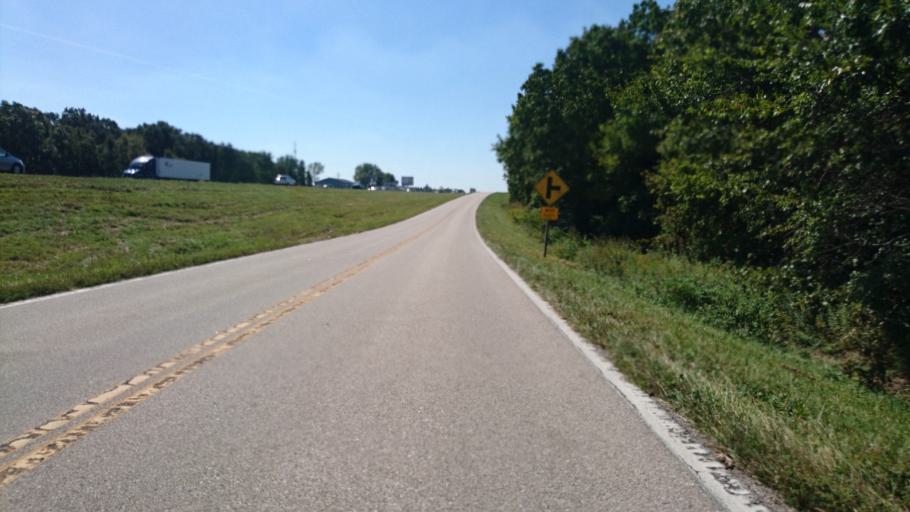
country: US
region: Missouri
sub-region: Franklin County
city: Sullivan
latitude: 38.2574
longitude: -91.1235
